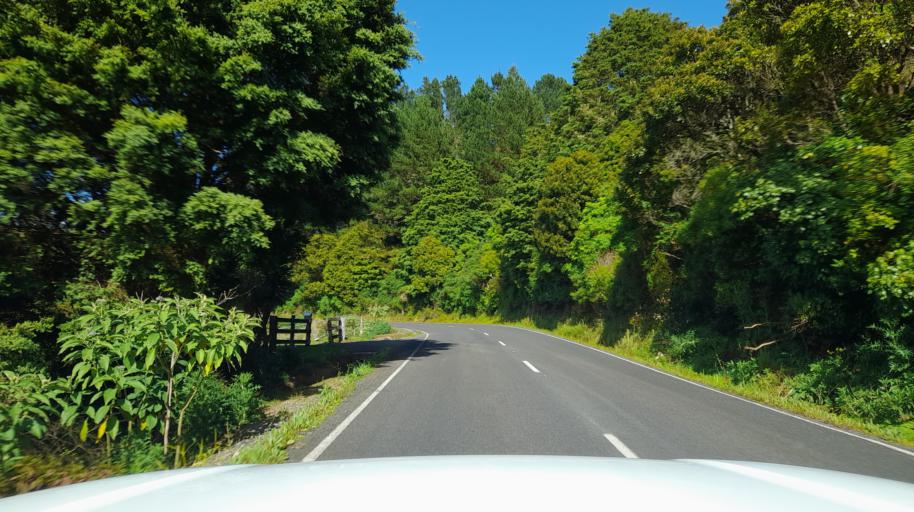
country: NZ
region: Northland
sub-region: Far North District
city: Moerewa
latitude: -35.4079
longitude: 173.9631
